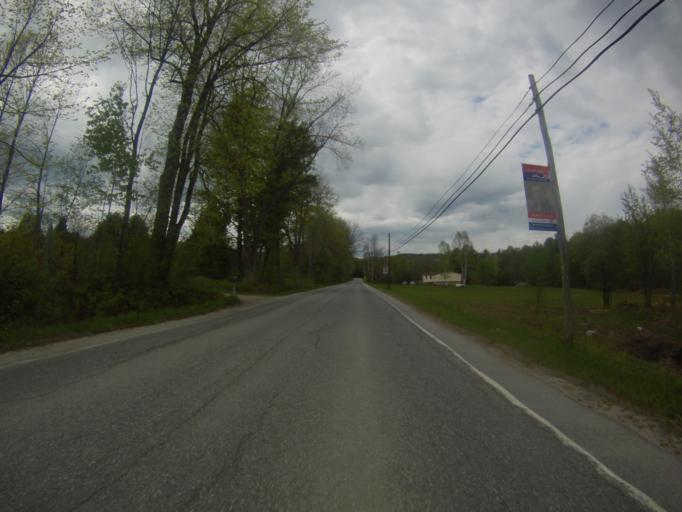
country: US
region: New York
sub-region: Essex County
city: Port Henry
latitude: 43.9518
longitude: -73.4810
